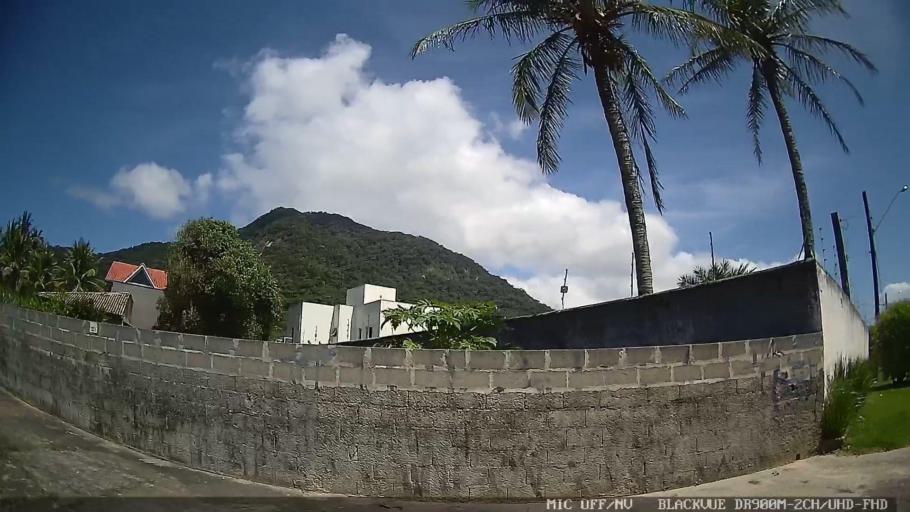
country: BR
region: Sao Paulo
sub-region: Peruibe
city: Peruibe
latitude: -24.3317
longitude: -47.0041
